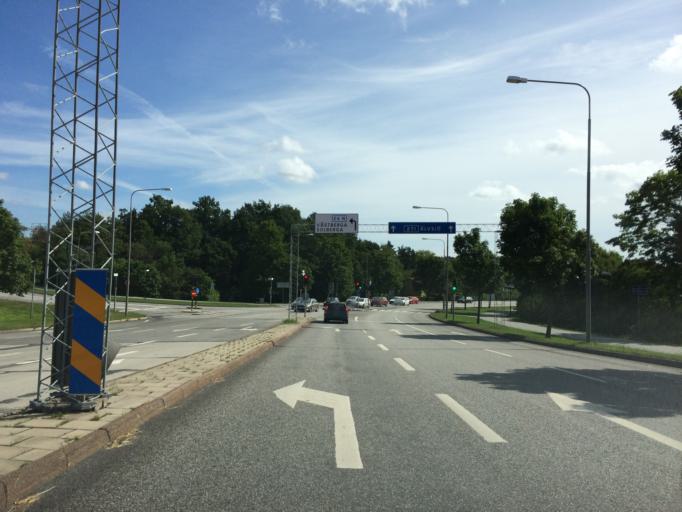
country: SE
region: Stockholm
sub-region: Huddinge Kommun
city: Huddinge
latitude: 59.2880
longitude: 17.9846
